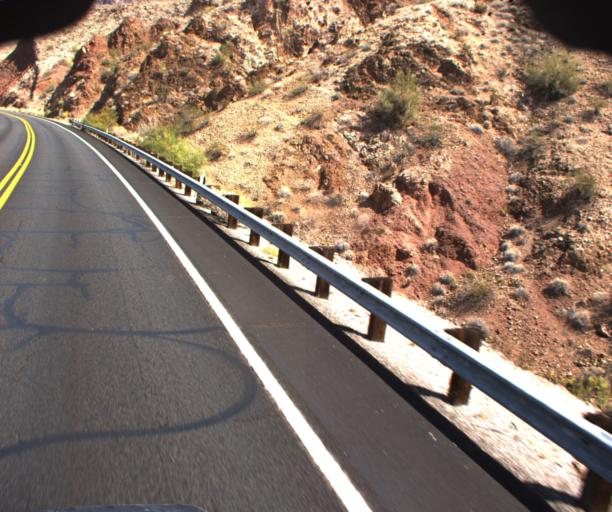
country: US
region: Arizona
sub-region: La Paz County
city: Cienega Springs
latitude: 34.2890
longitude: -114.1109
